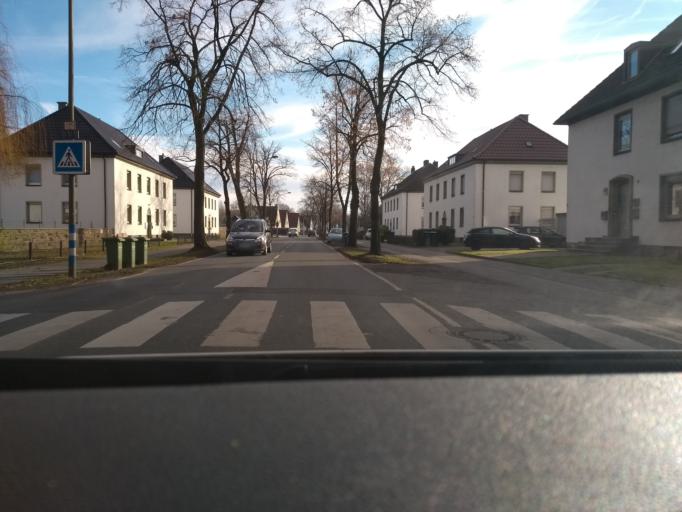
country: DE
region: North Rhine-Westphalia
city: Lunen
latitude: 51.6150
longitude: 7.5009
